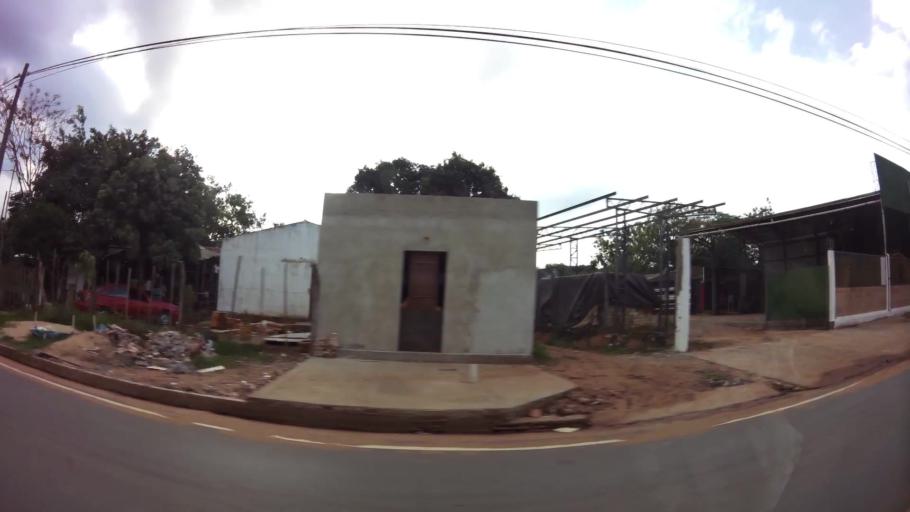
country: PY
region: Central
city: Nemby
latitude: -25.3706
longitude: -57.5428
